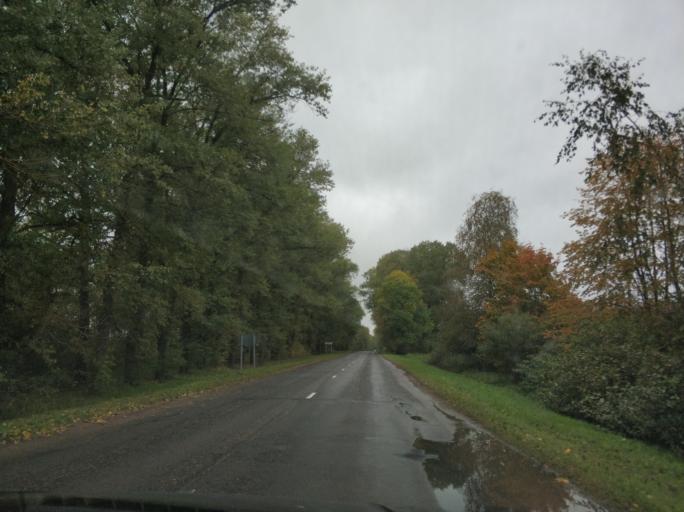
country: BY
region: Vitebsk
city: Polatsk
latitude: 55.4316
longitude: 28.9920
